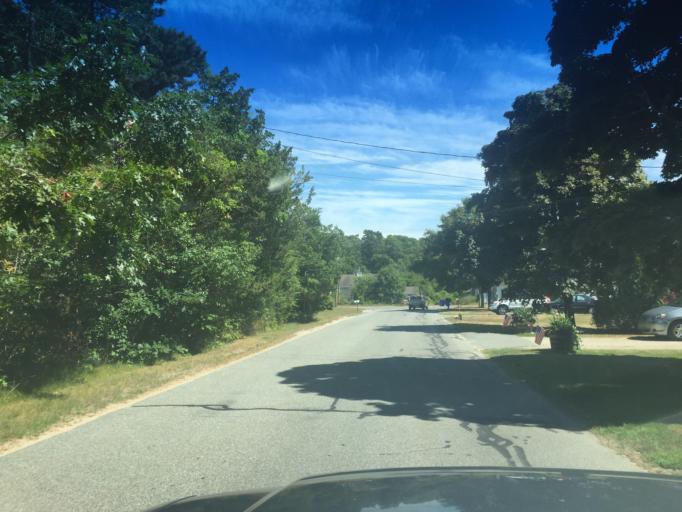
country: US
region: Massachusetts
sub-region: Barnstable County
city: Buzzards Bay
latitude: 41.7389
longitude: -70.6111
